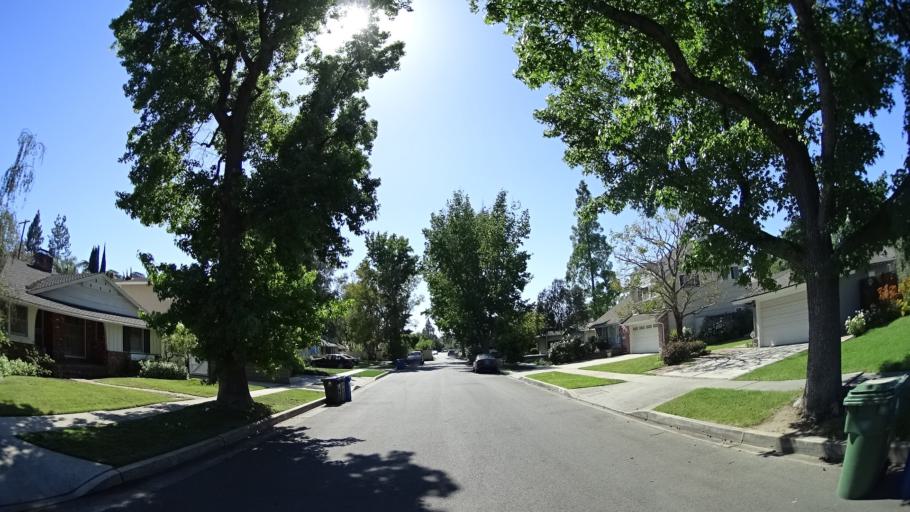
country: US
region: California
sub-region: Los Angeles County
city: Van Nuys
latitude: 34.1695
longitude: -118.4242
